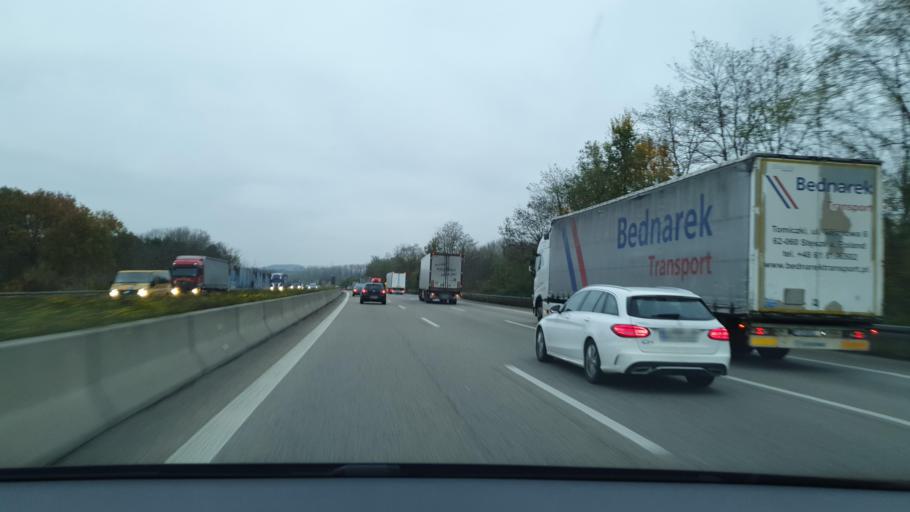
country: DE
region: Baden-Wuerttemberg
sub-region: Karlsruhe Region
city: Malsch
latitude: 49.2724
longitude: 8.6567
